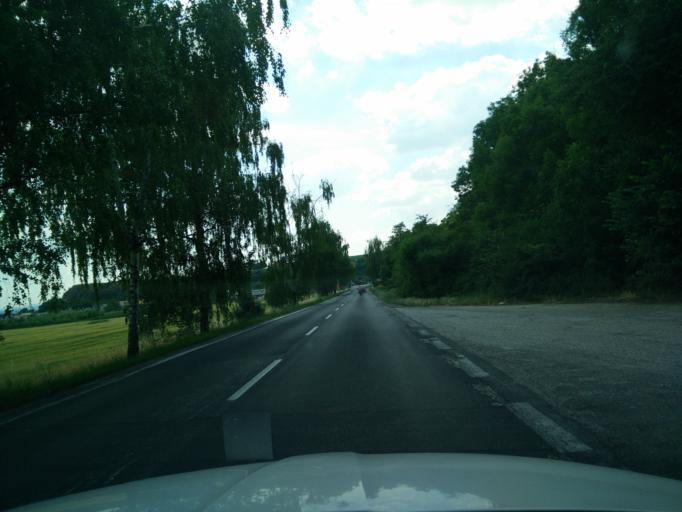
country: SK
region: Nitriansky
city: Partizanske
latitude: 48.6923
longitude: 18.3805
